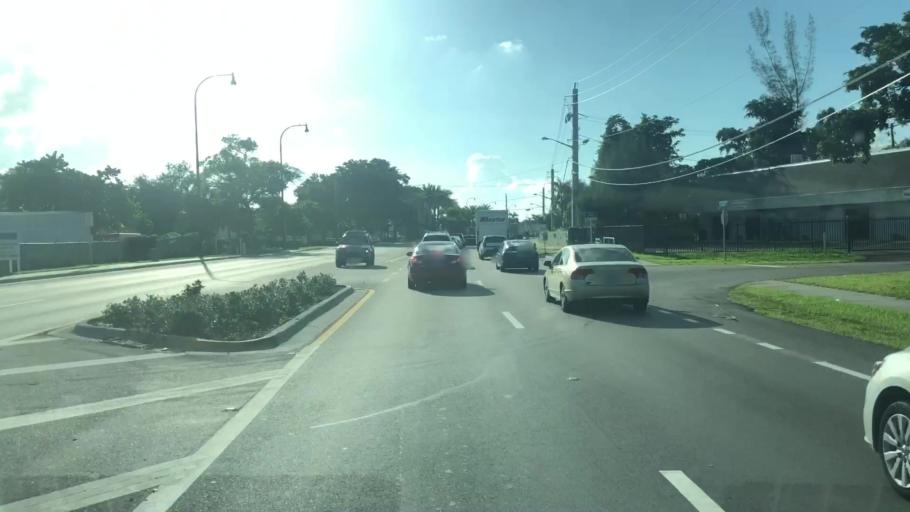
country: US
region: Florida
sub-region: Broward County
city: Coconut Creek
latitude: 26.2451
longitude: -80.1557
